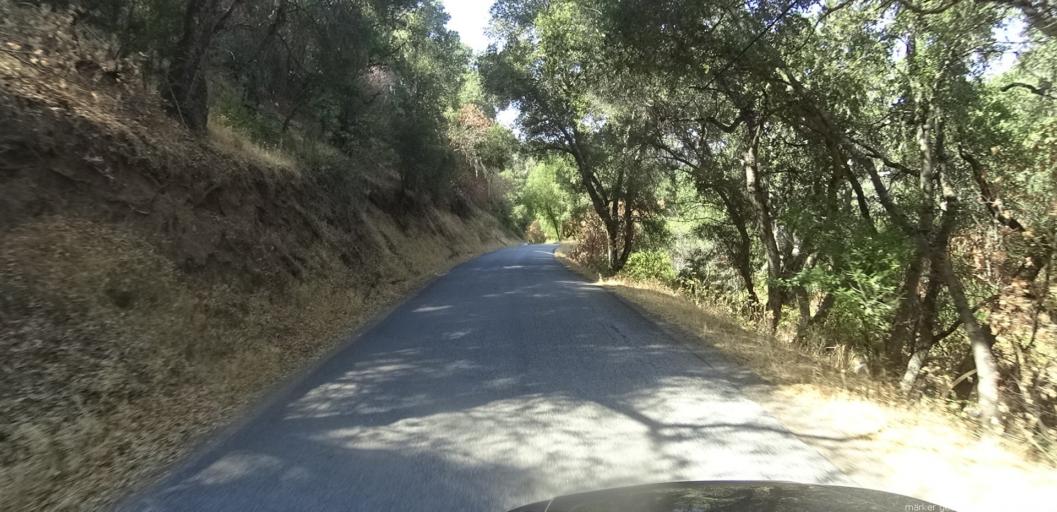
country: US
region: California
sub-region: Monterey County
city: Carmel Valley Village
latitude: 36.3934
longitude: -121.6145
